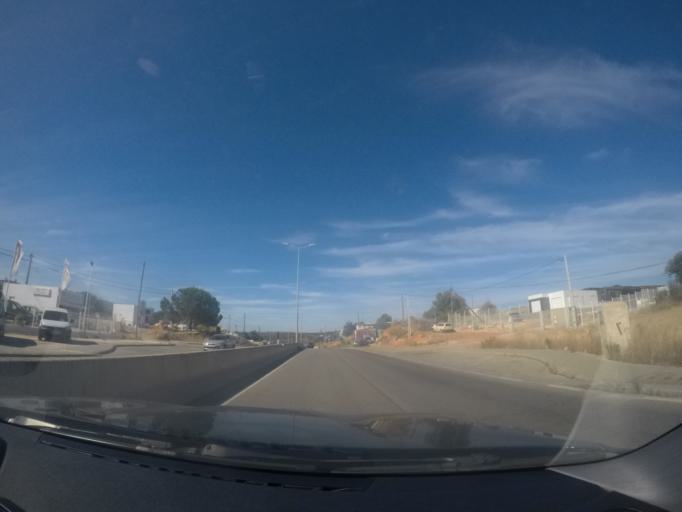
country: PT
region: Faro
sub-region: Portimao
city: Portimao
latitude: 37.1650
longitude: -8.5322
